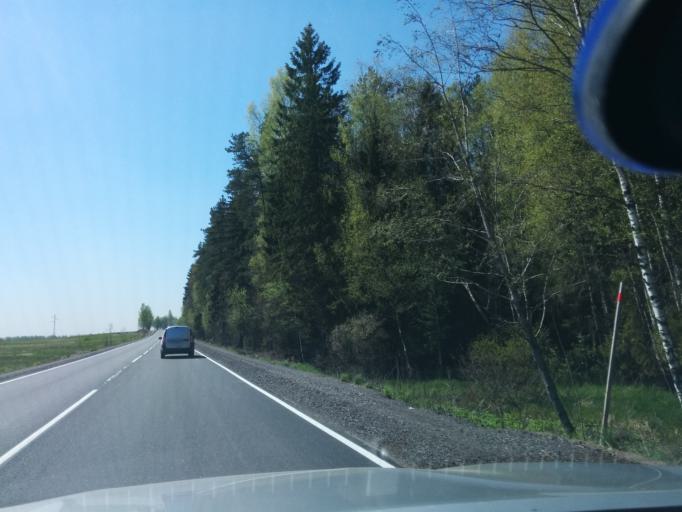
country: RU
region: Leningrad
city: Verkhniye Osel'ki
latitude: 60.1921
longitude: 30.4140
